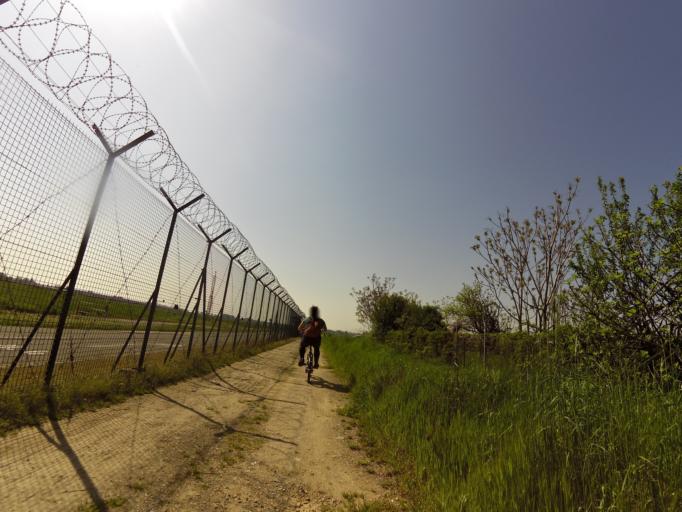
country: IT
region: Lombardy
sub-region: Citta metropolitana di Milano
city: Linate
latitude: 45.4453
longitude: 9.2748
